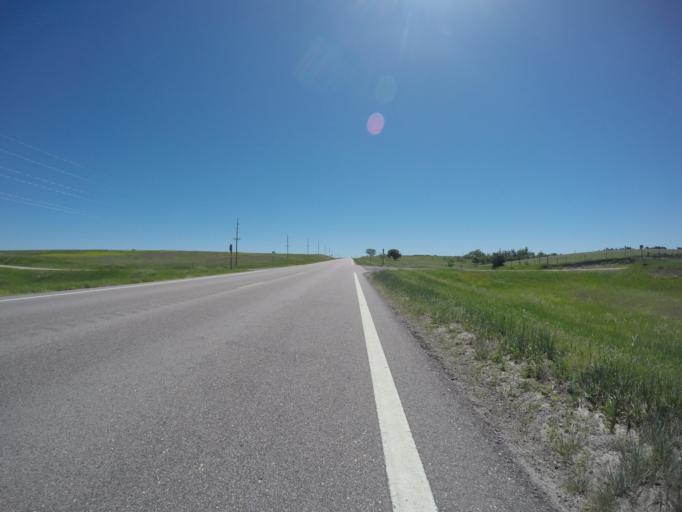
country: US
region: Kansas
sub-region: Norton County
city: Norton
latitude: 39.8284
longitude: -99.6651
